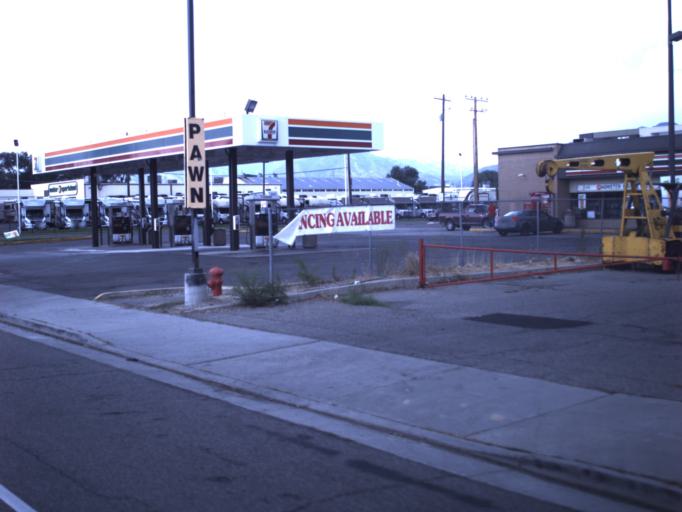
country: US
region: Utah
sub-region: Salt Lake County
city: Centerfield
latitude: 40.6830
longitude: -111.8882
